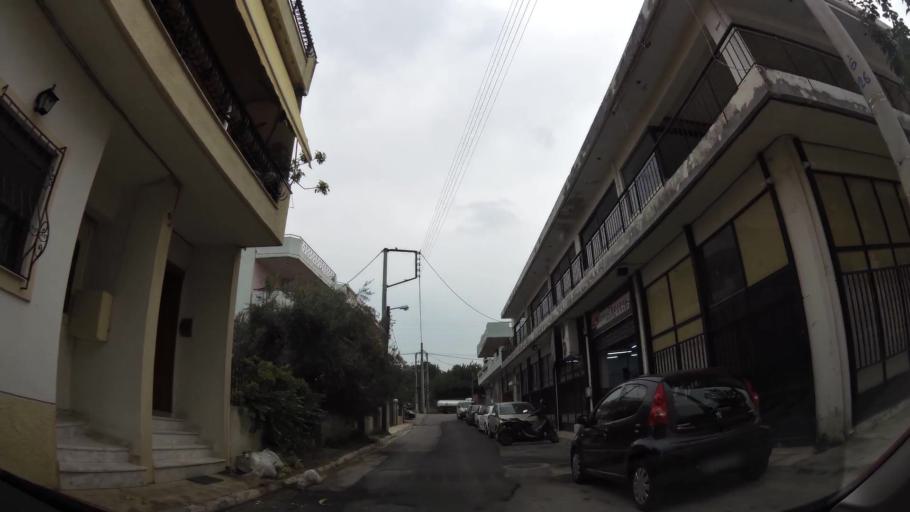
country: GR
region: Attica
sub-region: Nomarchia Athinas
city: Kamateron
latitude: 38.0462
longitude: 23.7148
